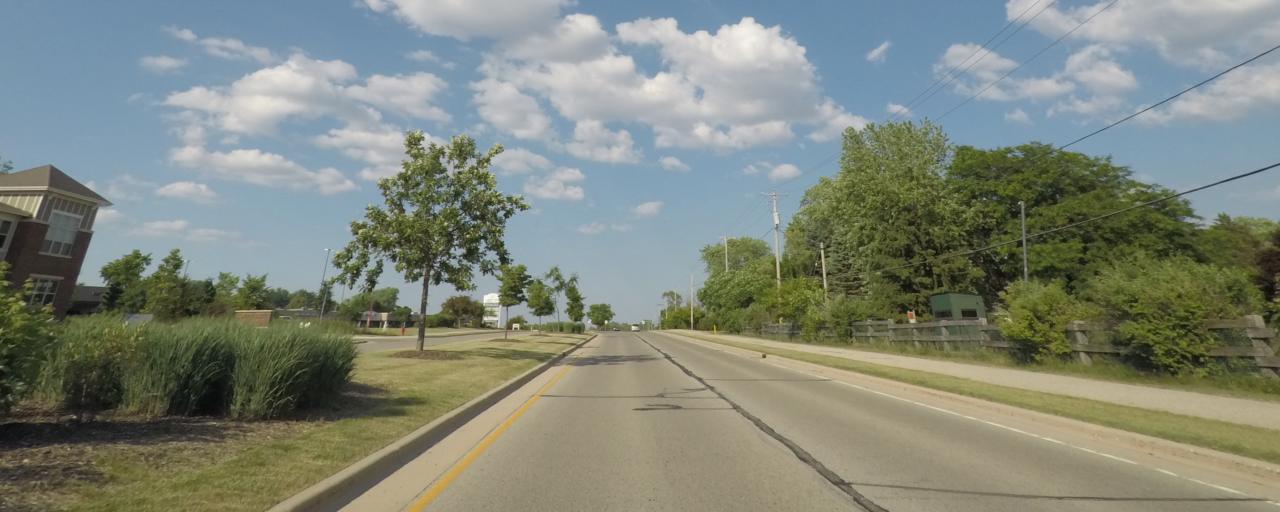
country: US
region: Wisconsin
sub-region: Milwaukee County
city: Hales Corners
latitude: 42.9275
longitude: -88.0867
